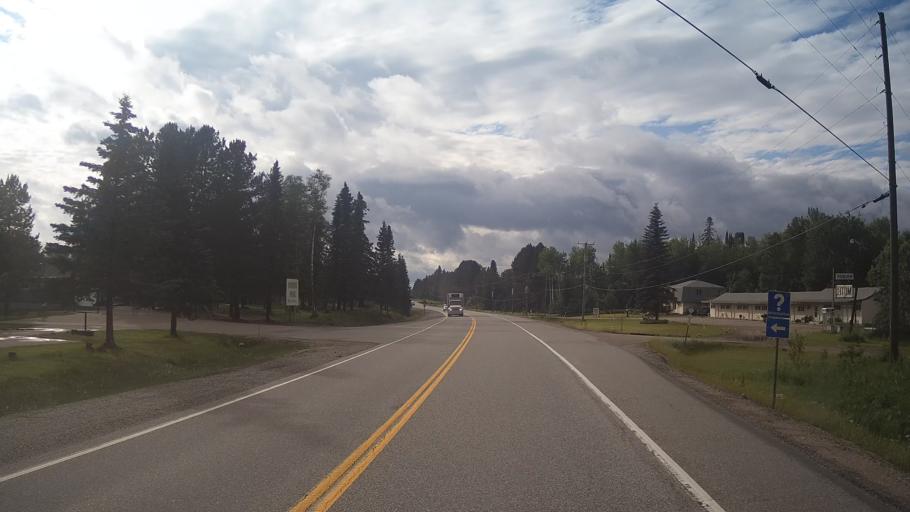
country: CA
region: Ontario
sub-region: Rainy River District
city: Atikokan
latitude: 49.0205
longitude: -90.4416
